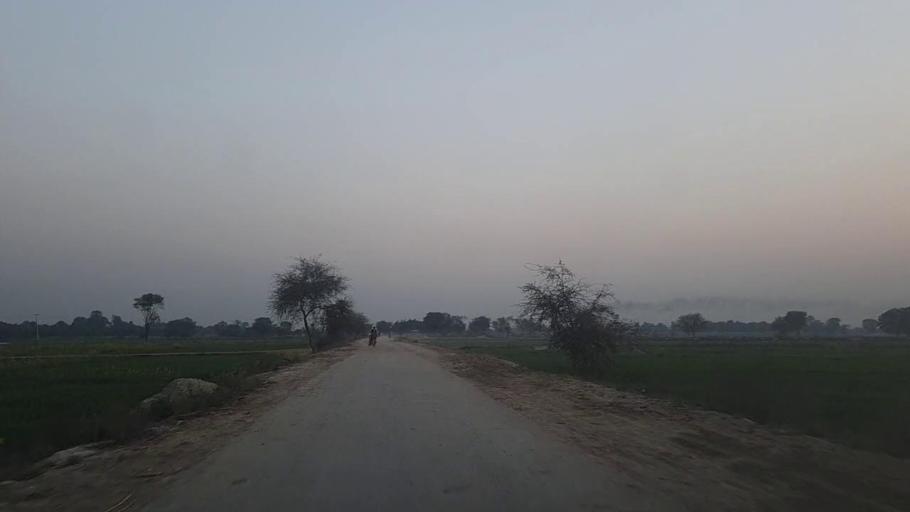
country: PK
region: Sindh
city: Naushahro Firoz
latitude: 26.8593
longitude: 68.0481
